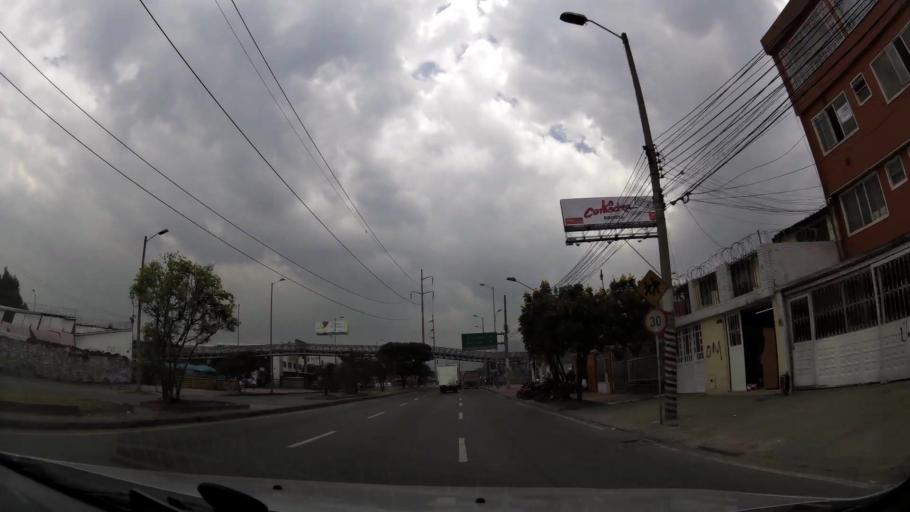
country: CO
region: Bogota D.C.
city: Bogota
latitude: 4.5968
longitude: -74.1092
